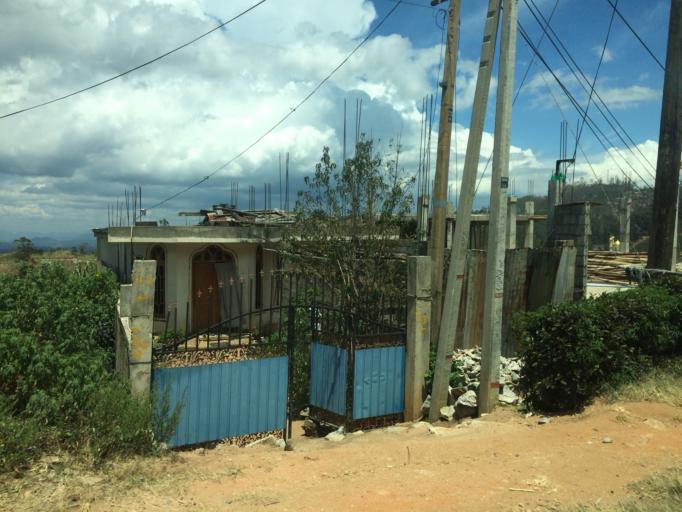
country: LK
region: Central
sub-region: Nuwara Eliya District
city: Nuwara Eliya
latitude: 6.9075
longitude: 80.8421
